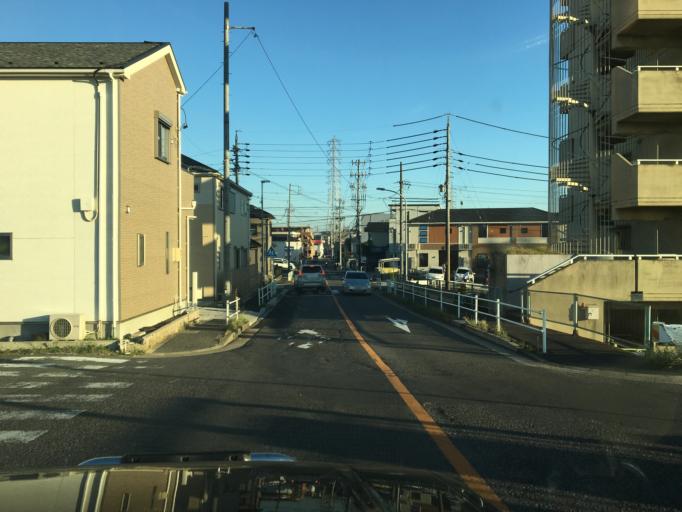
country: JP
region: Aichi
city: Kasugai
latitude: 35.1992
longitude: 137.0012
